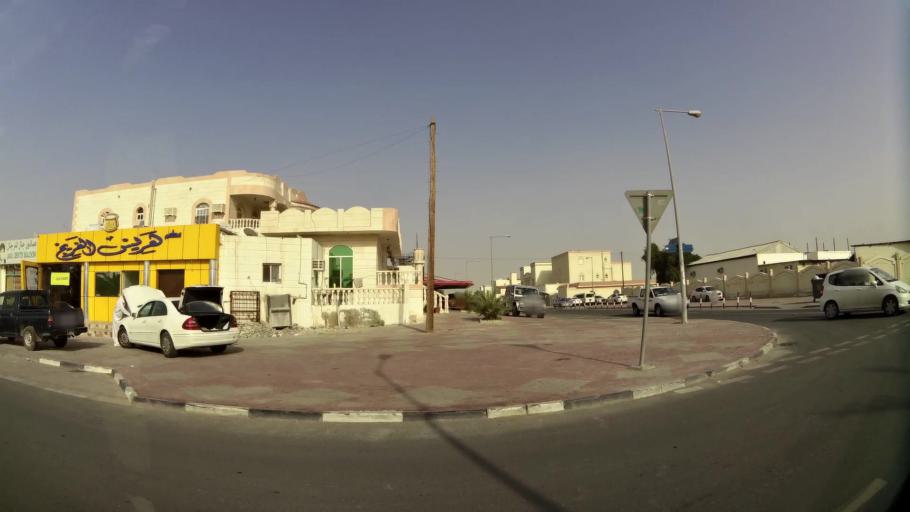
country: QA
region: Baladiyat ar Rayyan
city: Ar Rayyan
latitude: 25.2370
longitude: 51.4318
